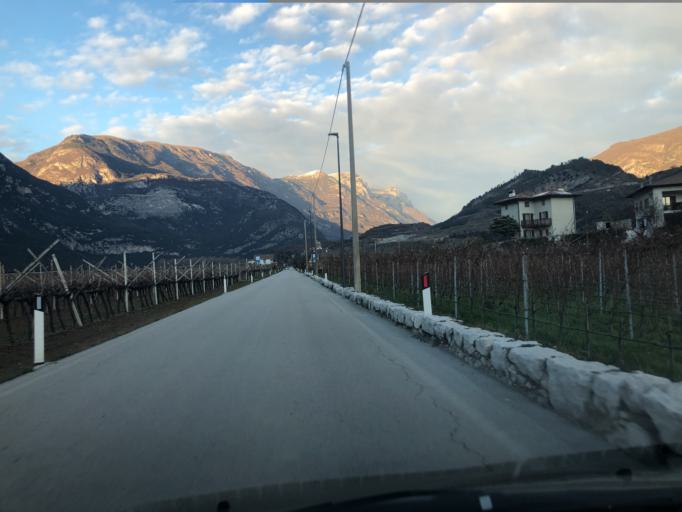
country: IT
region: Trentino-Alto Adige
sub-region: Provincia di Trento
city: Pietramurata
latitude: 46.0294
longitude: 10.9584
